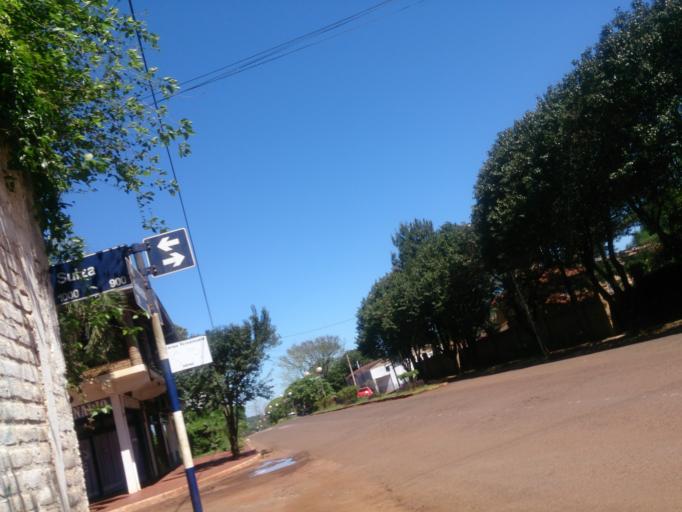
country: AR
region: Misiones
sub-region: Departamento de Obera
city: Obera
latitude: -27.4914
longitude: -55.1099
